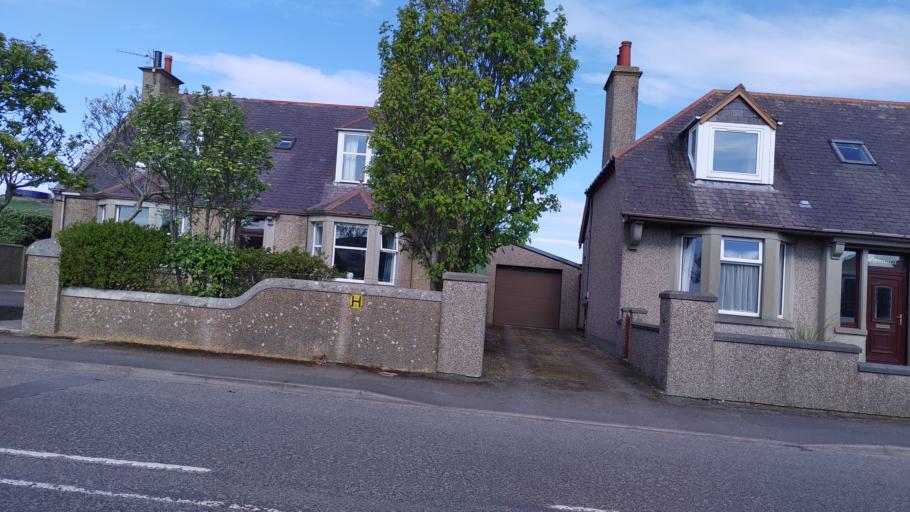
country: GB
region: Scotland
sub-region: Orkney Islands
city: Orkney
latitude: 58.9752
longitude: -2.9701
